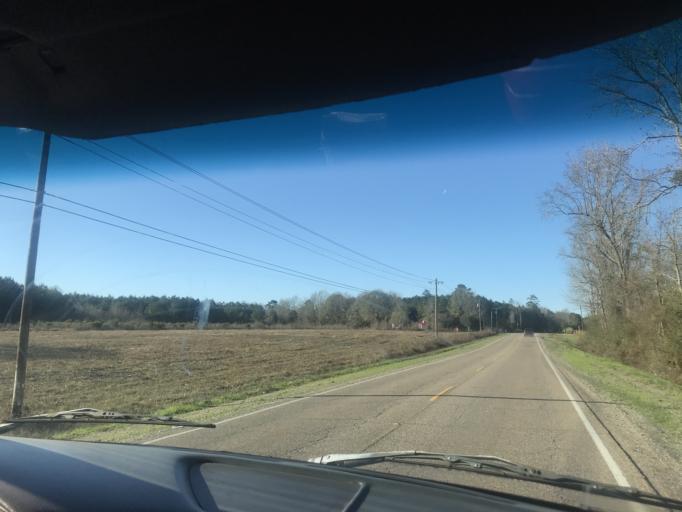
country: US
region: Louisiana
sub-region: Saint Tammany Parish
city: Covington
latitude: 30.5964
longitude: -90.1769
